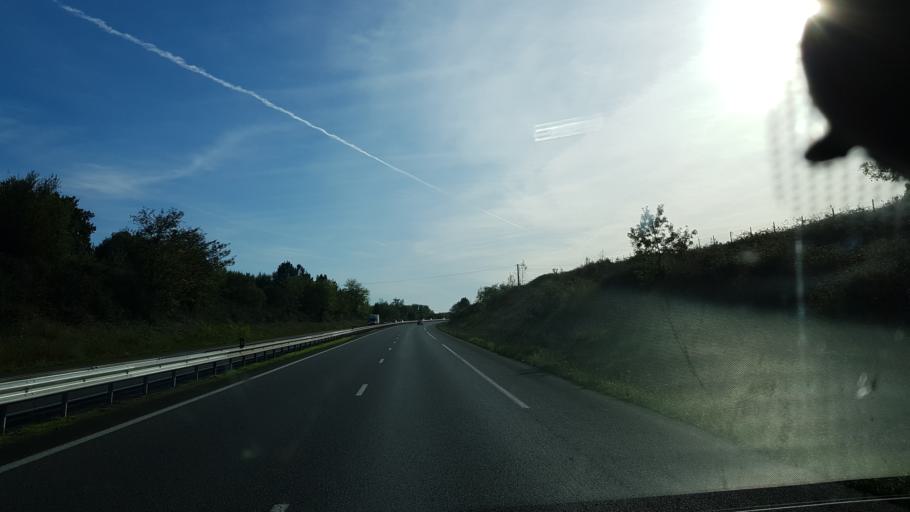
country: FR
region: Poitou-Charentes
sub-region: Departement de la Charente-Maritime
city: Montlieu-la-Garde
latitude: 45.2673
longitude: -0.2476
